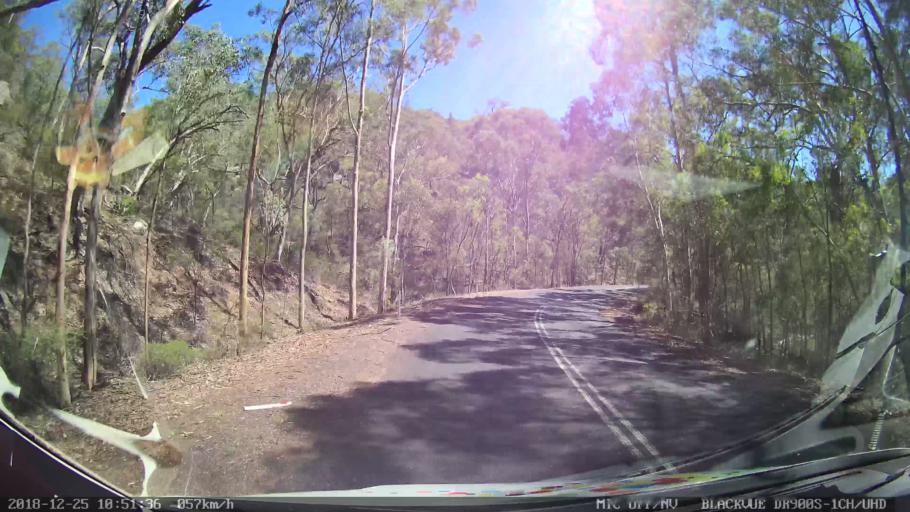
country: AU
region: New South Wales
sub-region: Upper Hunter Shire
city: Merriwa
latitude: -32.4354
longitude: 150.2695
